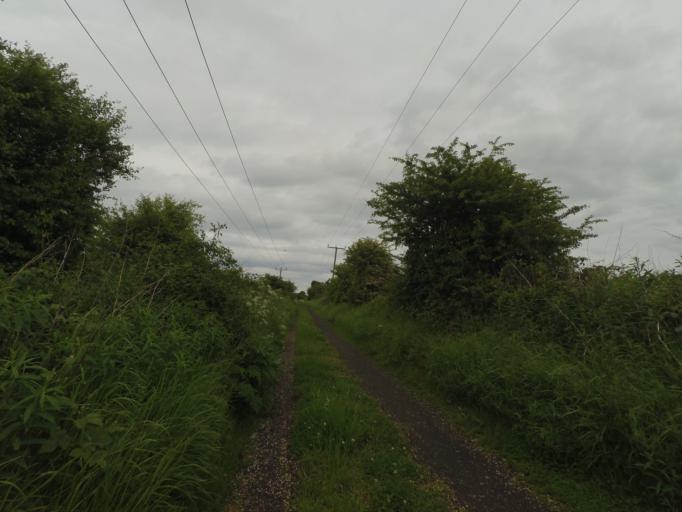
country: GB
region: Scotland
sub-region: East Lothian
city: Macmerry
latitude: 55.9257
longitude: -2.9091
